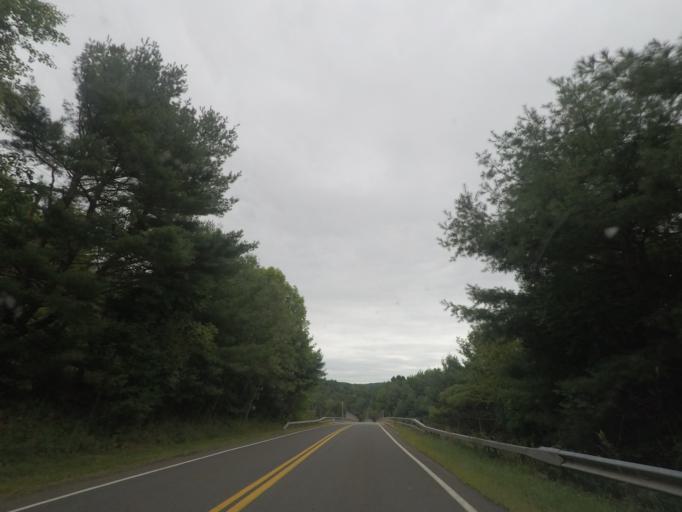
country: US
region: New York
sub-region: Rensselaer County
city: Nassau
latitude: 42.4479
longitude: -73.5682
